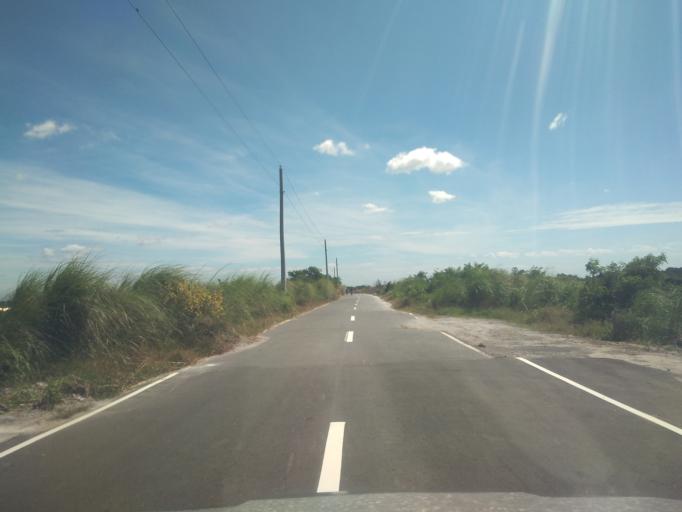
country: PH
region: Central Luzon
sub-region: Province of Pampanga
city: Balas
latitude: 15.0545
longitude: 120.5747
